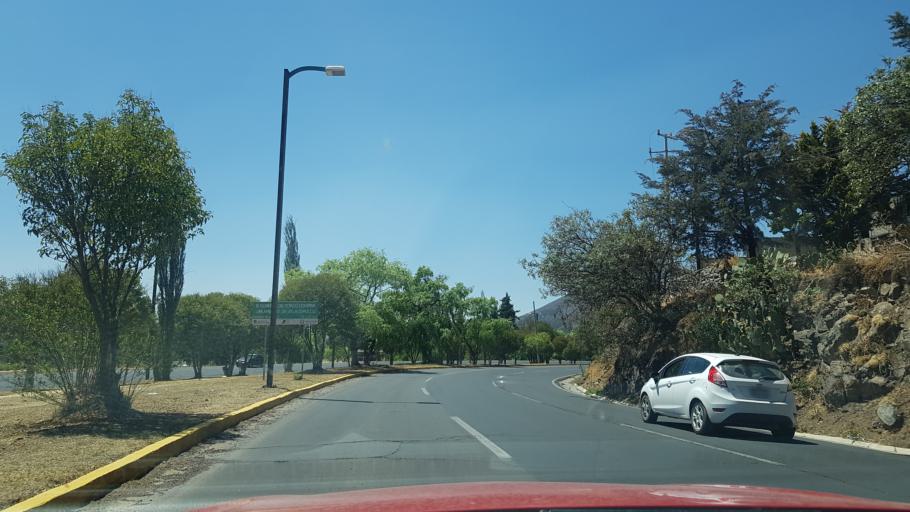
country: MX
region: Mexico
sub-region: Atlacomulco
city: Santa Cruz Bombatevi
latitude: 19.8002
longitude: -99.8867
